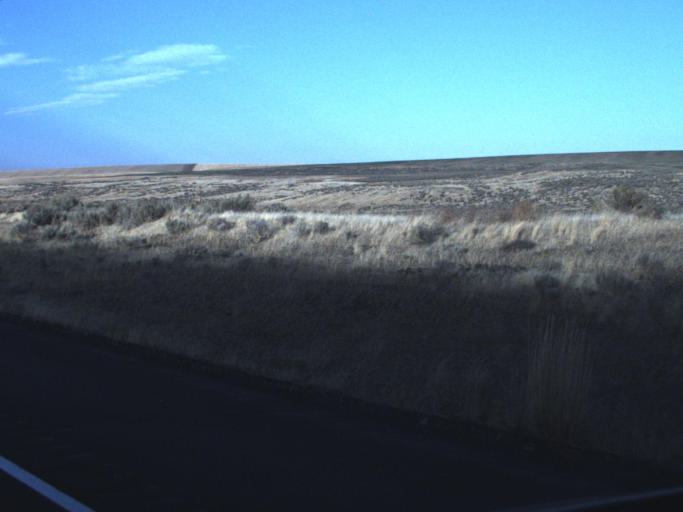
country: US
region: Washington
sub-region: Adams County
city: Ritzville
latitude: 47.0532
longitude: -118.4236
